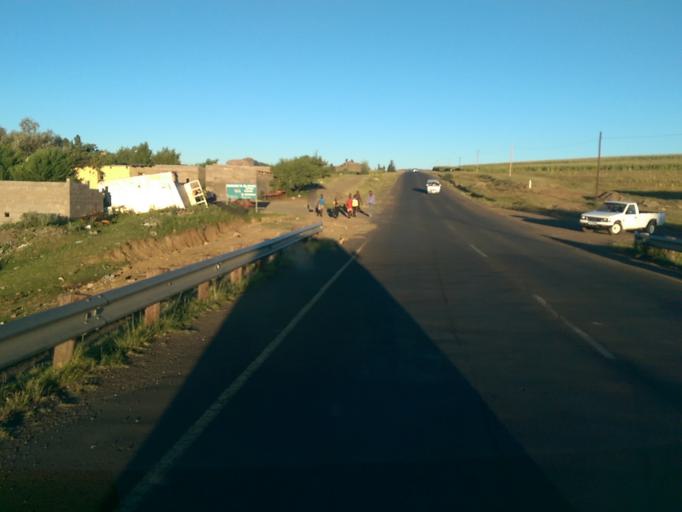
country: LS
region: Maseru
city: Maseru
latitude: -29.4083
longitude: 27.5969
